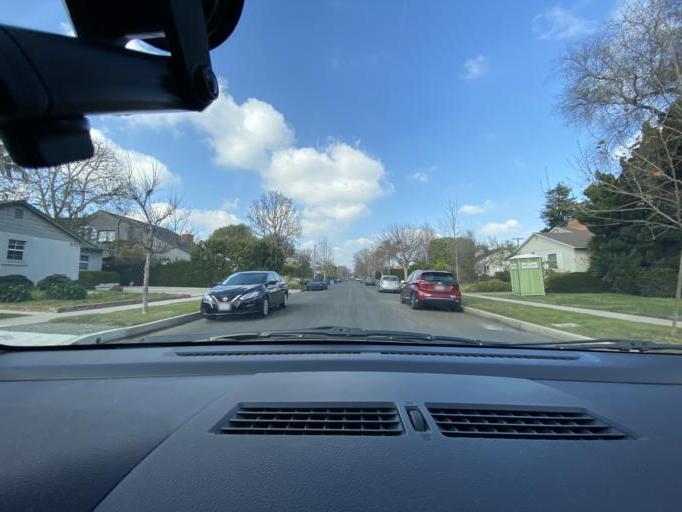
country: US
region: California
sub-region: Los Angeles County
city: Culver City
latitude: 34.0191
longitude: -118.4318
